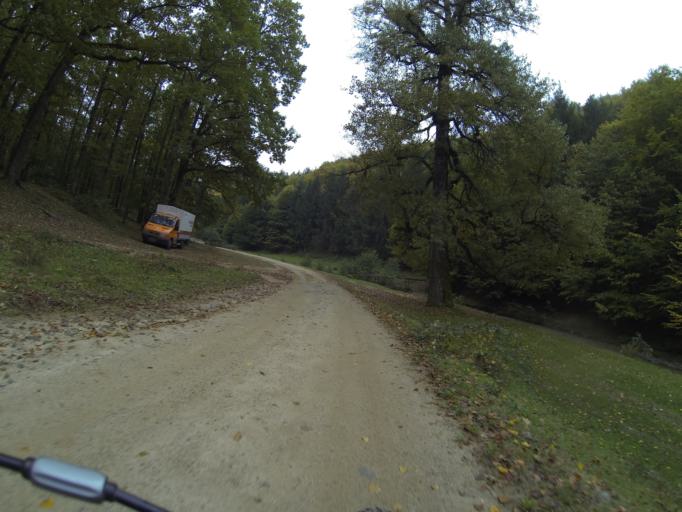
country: RO
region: Gorj
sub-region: Comuna Tismana
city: Sohodol
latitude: 45.0636
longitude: 22.8935
